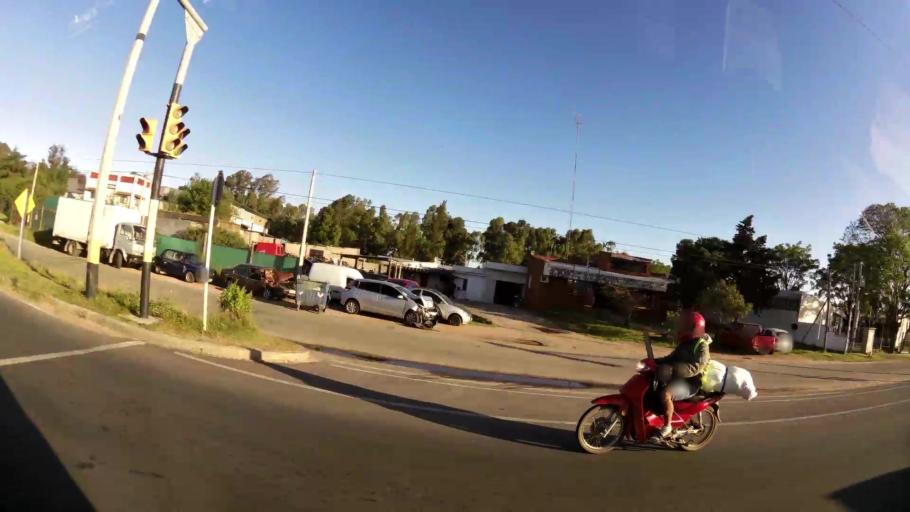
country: UY
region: Canelones
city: Paso de Carrasco
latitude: -34.8567
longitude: -56.0455
